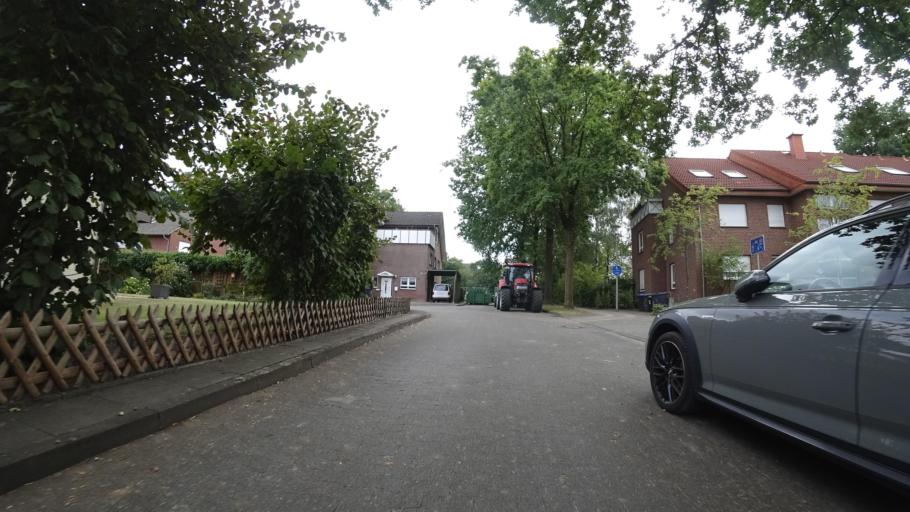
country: DE
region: North Rhine-Westphalia
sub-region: Regierungsbezirk Detmold
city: Verl
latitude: 51.9393
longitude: 8.4667
